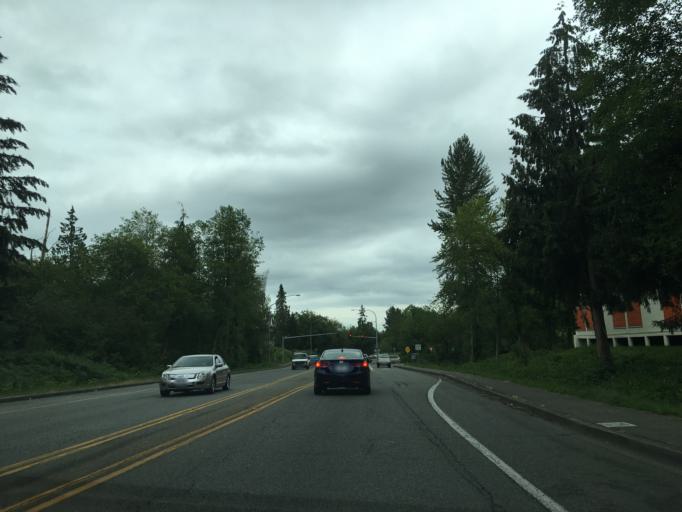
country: US
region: Washington
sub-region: Snohomish County
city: Alderwood Manor
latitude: 47.8427
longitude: -122.2711
